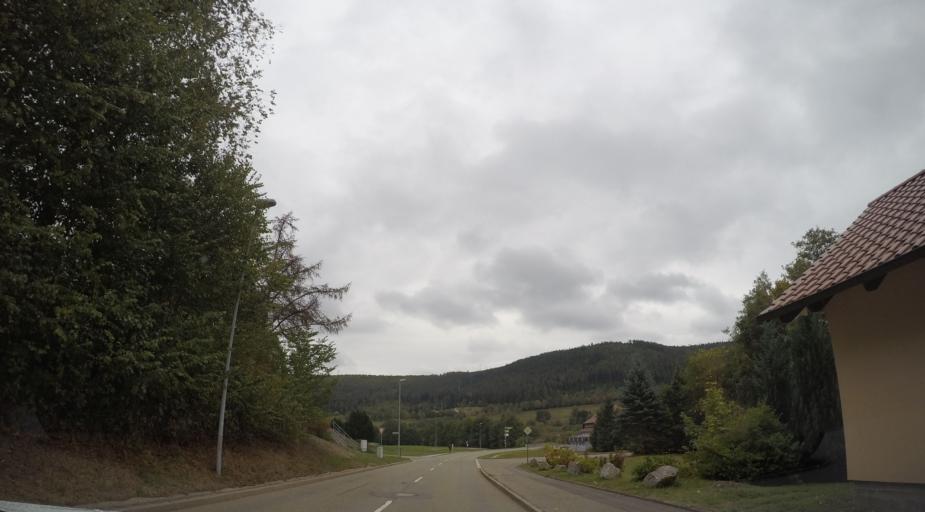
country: DE
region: Baden-Wuerttemberg
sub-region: Karlsruhe Region
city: Baiersbronn
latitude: 48.5193
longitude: 8.3769
